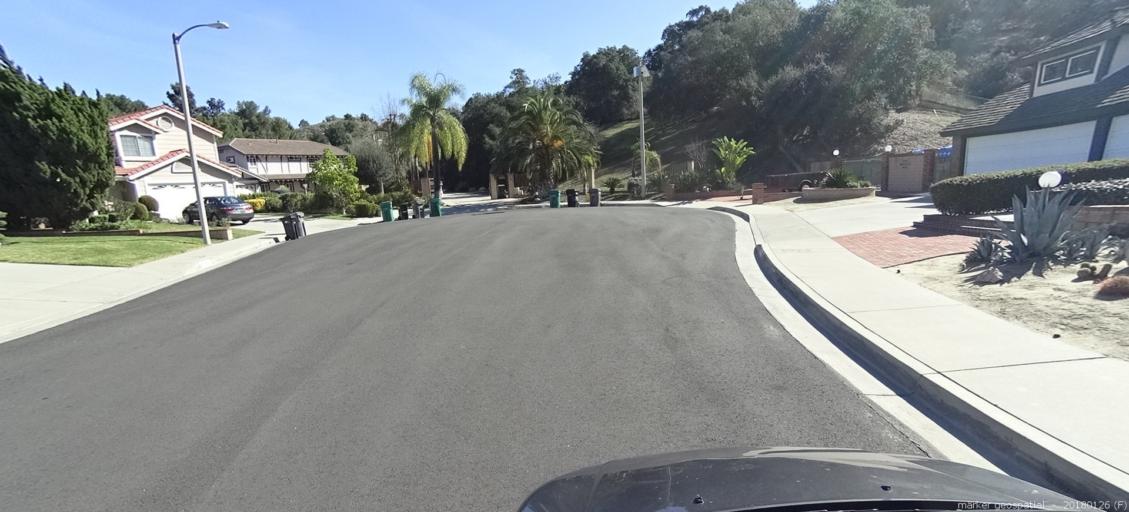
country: US
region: California
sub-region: Los Angeles County
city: Walnut
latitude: 33.9943
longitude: -117.8500
